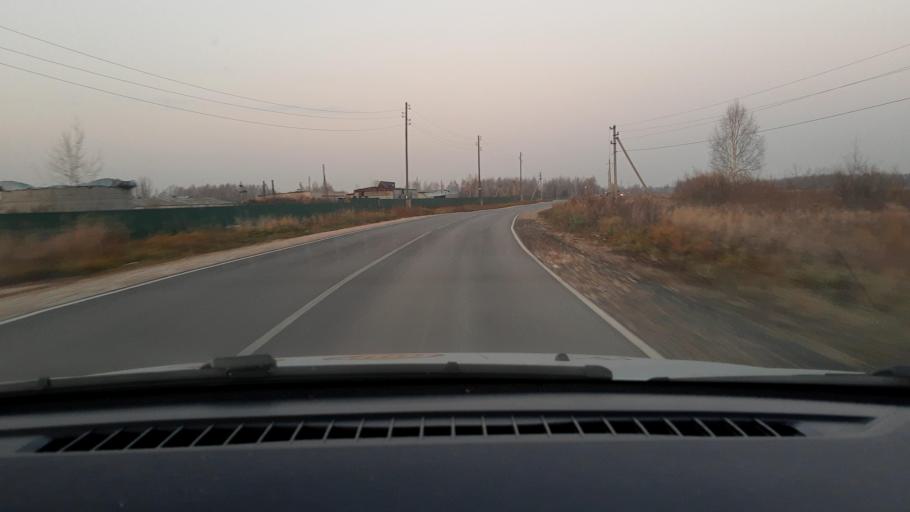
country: RU
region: Nizjnij Novgorod
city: Neklyudovo
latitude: 56.4500
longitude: 43.9005
